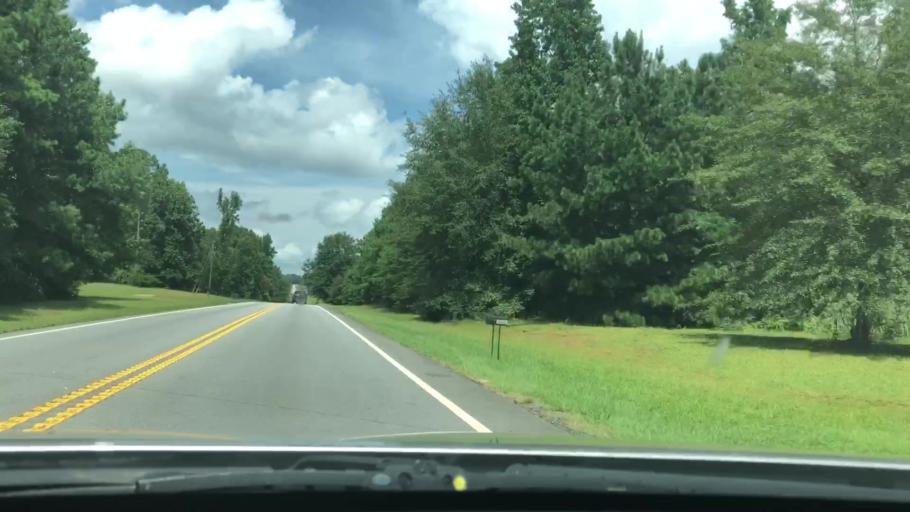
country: US
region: Georgia
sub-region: Lamar County
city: Barnesville
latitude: 33.1179
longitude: -84.1542
